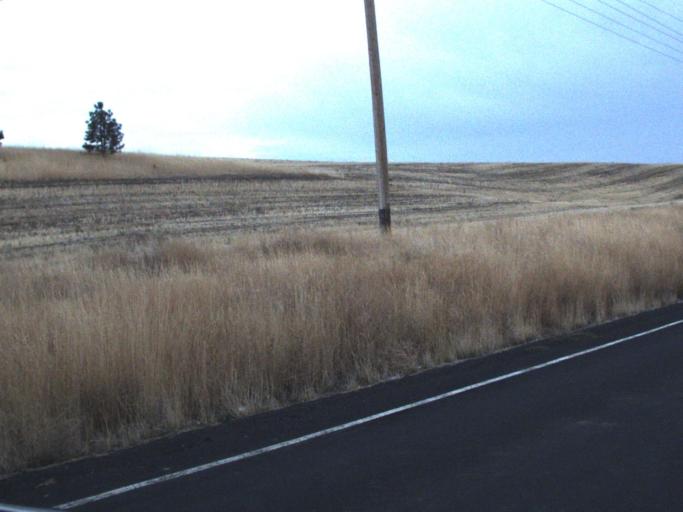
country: US
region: Washington
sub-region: Lincoln County
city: Davenport
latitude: 47.8312
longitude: -118.2090
